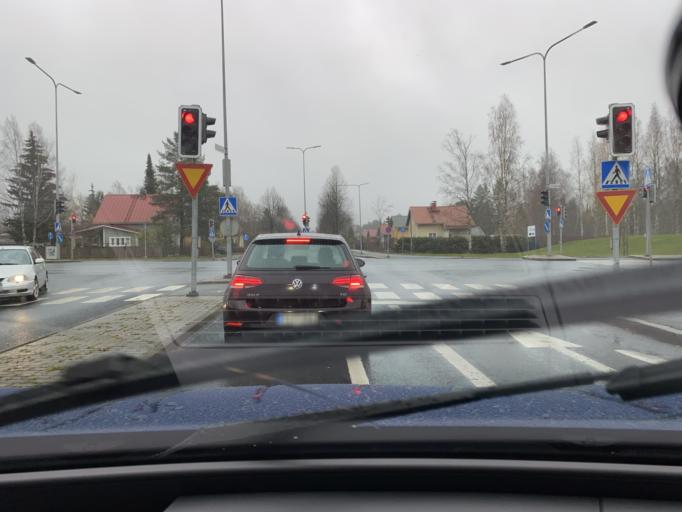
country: FI
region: Haeme
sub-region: Forssa
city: Forssa
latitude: 60.8076
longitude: 23.6220
